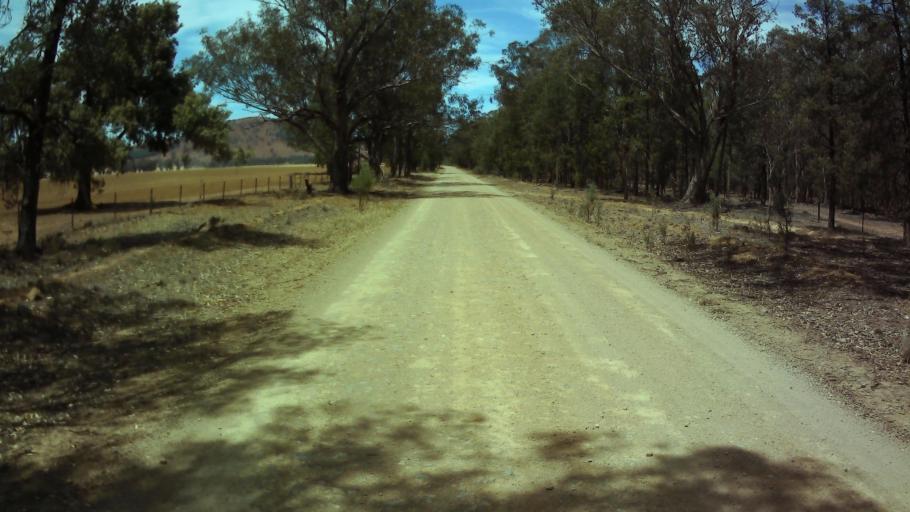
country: AU
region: New South Wales
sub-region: Weddin
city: Grenfell
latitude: -33.7617
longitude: 148.1249
